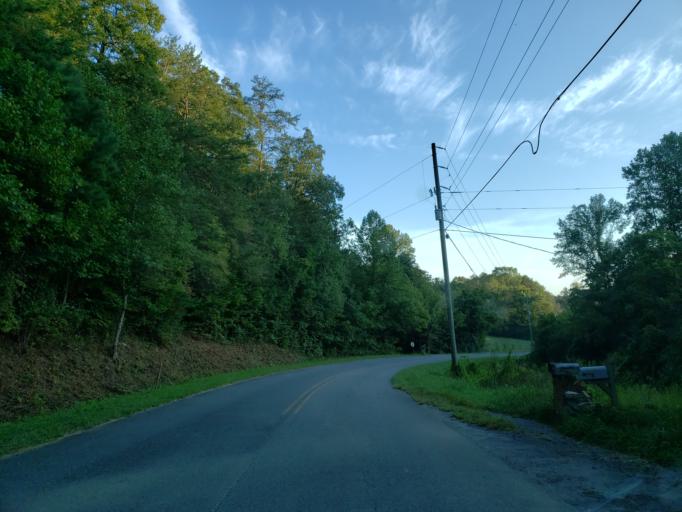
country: US
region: Georgia
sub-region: Gilmer County
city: Ellijay
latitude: 34.6723
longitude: -84.3297
